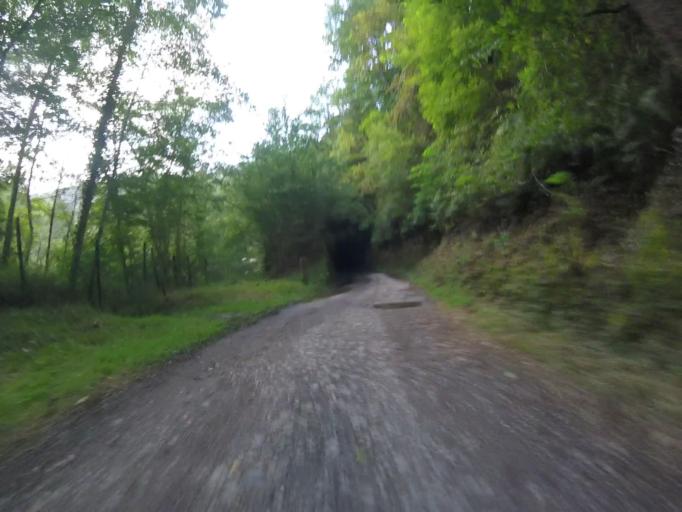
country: ES
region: Basque Country
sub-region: Provincia de Guipuzcoa
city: Berastegui
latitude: 43.1679
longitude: -1.9599
